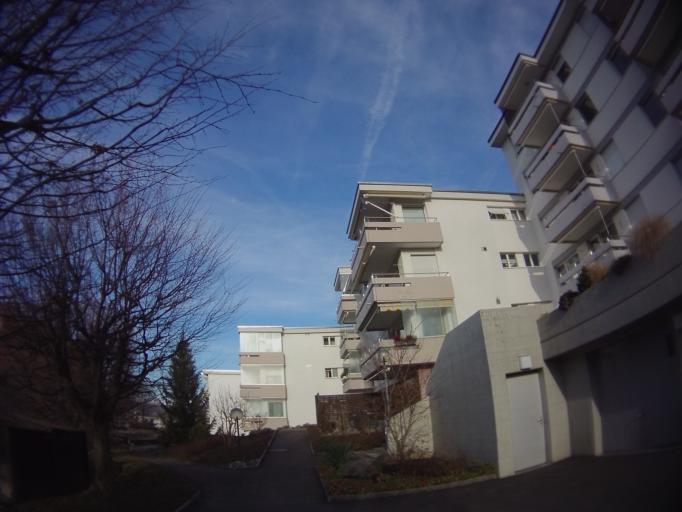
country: CH
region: Zug
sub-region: Zug
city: Baar
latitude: 47.1806
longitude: 8.5359
